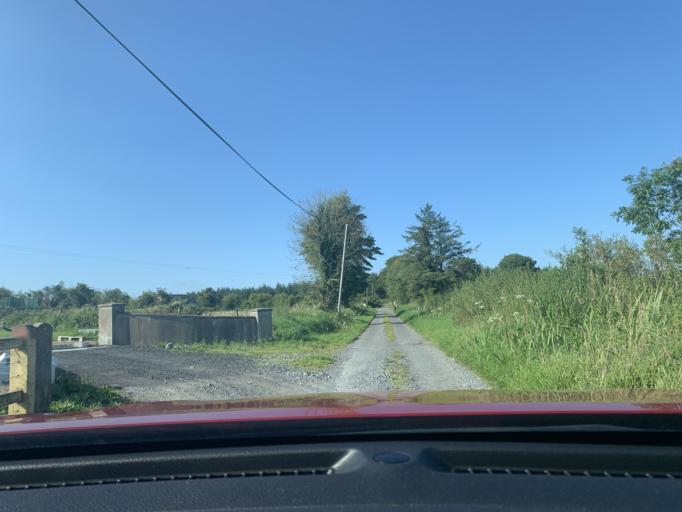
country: IE
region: Connaught
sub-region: Sligo
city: Tobercurry
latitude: 54.0585
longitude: -8.7936
